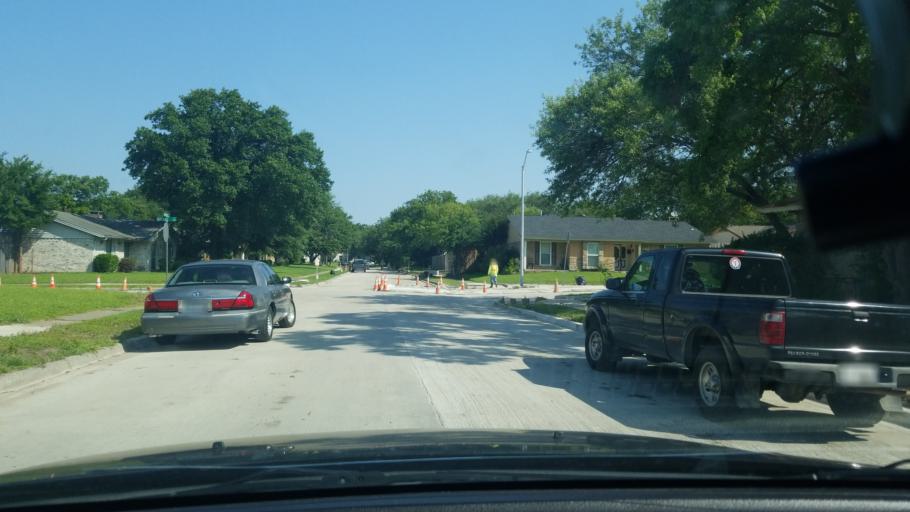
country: US
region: Texas
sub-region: Dallas County
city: Mesquite
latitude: 32.8160
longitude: -96.6454
